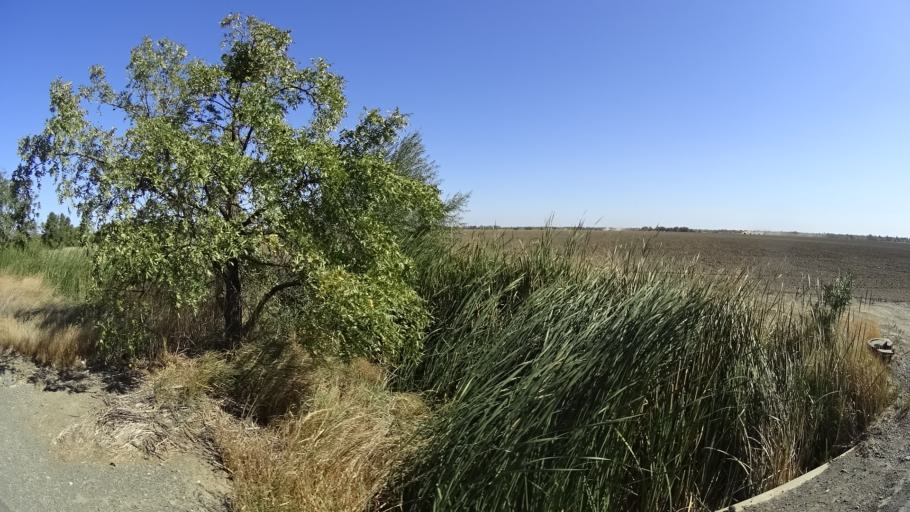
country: US
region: California
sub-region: Yolo County
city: Davis
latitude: 38.5738
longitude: -121.8032
